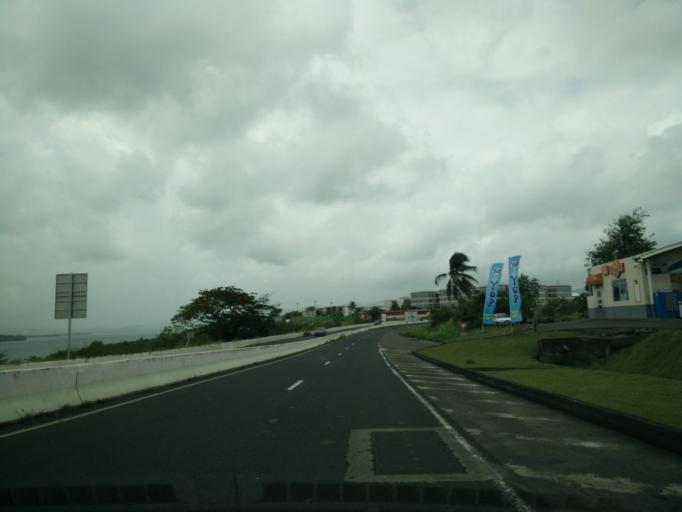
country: MQ
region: Martinique
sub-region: Martinique
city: Fort-de-France
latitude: 14.6069
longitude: -61.0423
